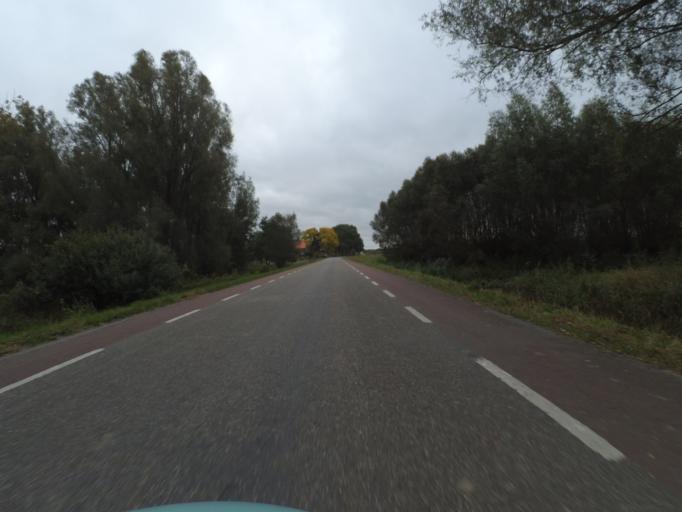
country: NL
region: Gelderland
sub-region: Gemeente Buren
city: Lienden
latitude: 51.9498
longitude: 5.5270
